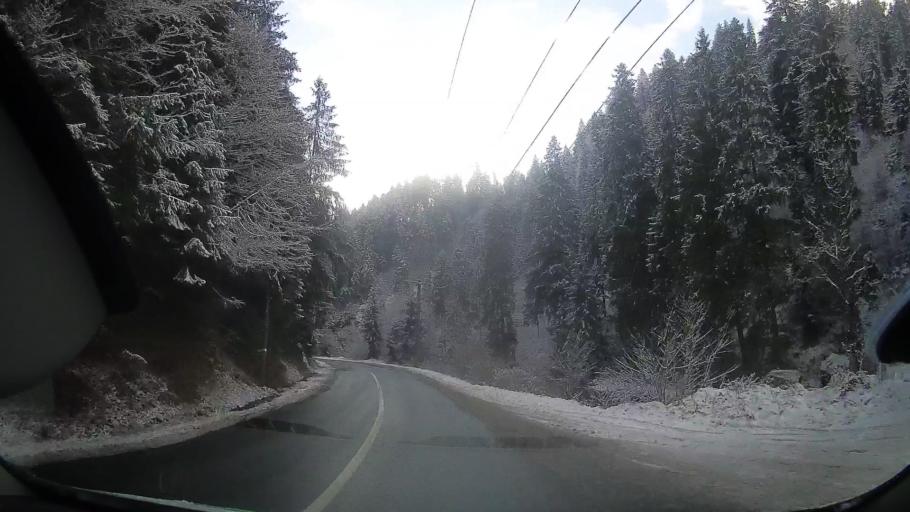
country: RO
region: Alba
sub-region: Comuna Scarisoara
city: Scarisoara
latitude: 46.4571
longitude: 22.8506
